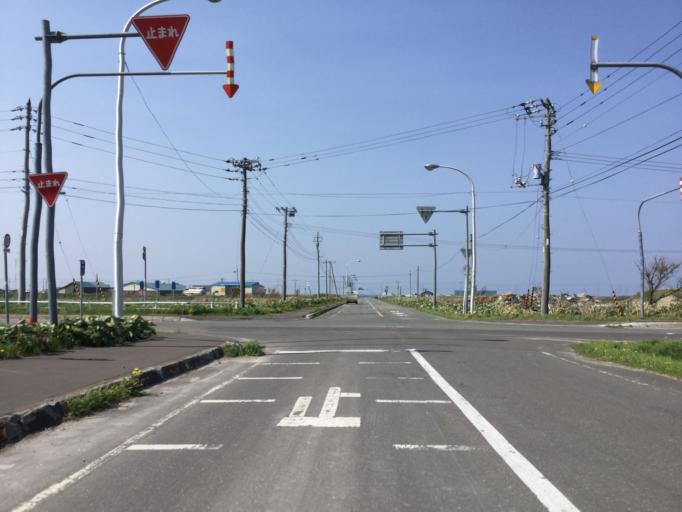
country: JP
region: Hokkaido
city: Makubetsu
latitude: 45.3989
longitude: 141.7670
